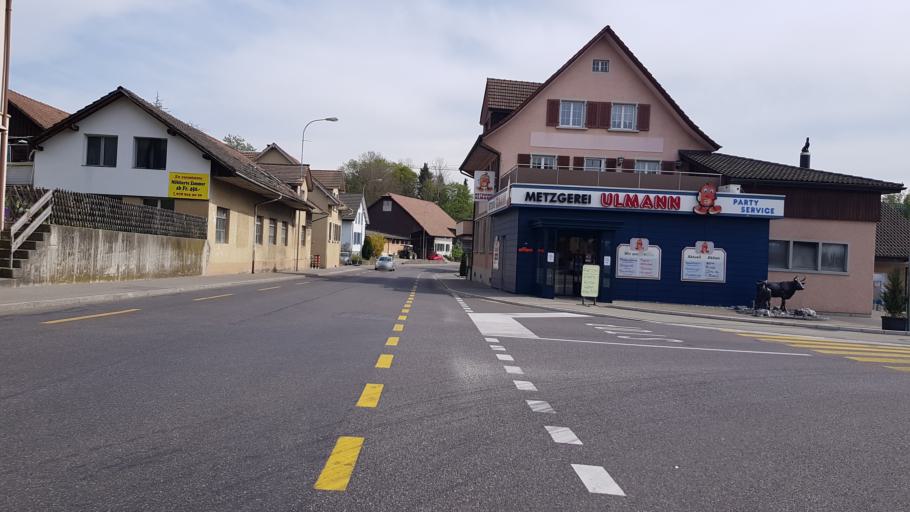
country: CH
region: Aargau
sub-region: Bezirk Kulm
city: Gontenschwil
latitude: 47.2846
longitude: 8.1523
